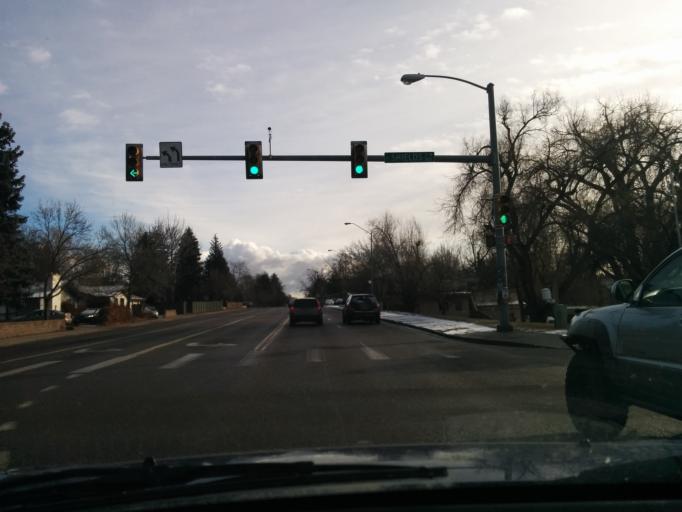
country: US
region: Colorado
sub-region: Larimer County
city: Fort Collins
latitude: 40.5672
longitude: -105.0961
